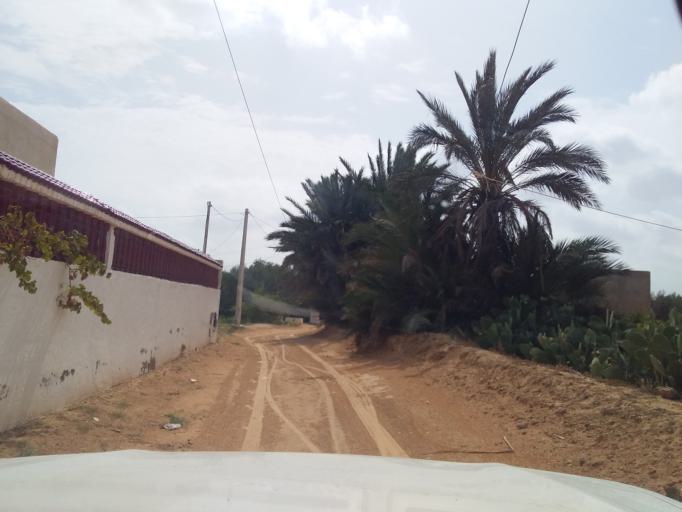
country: TN
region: Qabis
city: Gabes
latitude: 33.6275
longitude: 10.3111
